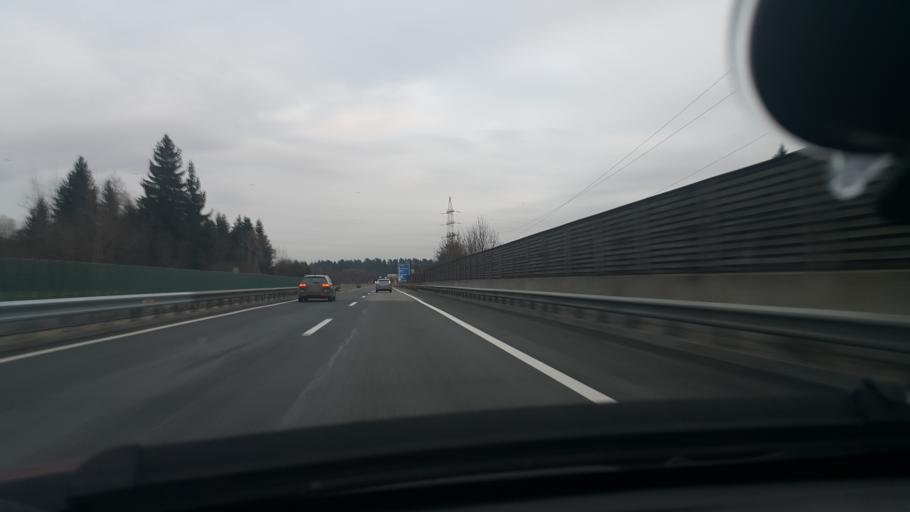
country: AT
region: Carinthia
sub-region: Politischer Bezirk Klagenfurt Land
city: Poggersdorf
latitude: 46.6449
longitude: 14.4191
